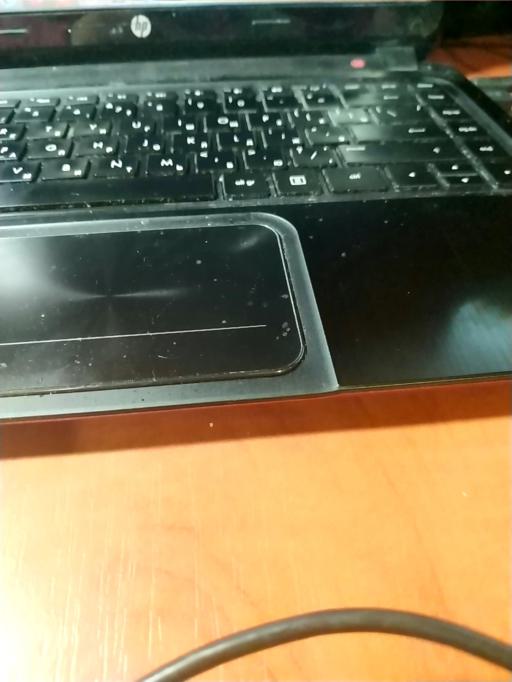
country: RU
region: Tverskaya
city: Likhoslavl'
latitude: 57.1878
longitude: 35.5238
